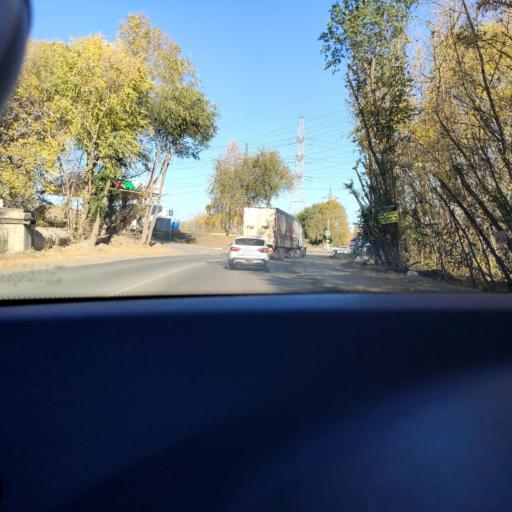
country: RU
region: Samara
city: Petra-Dubrava
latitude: 53.2561
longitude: 50.2962
